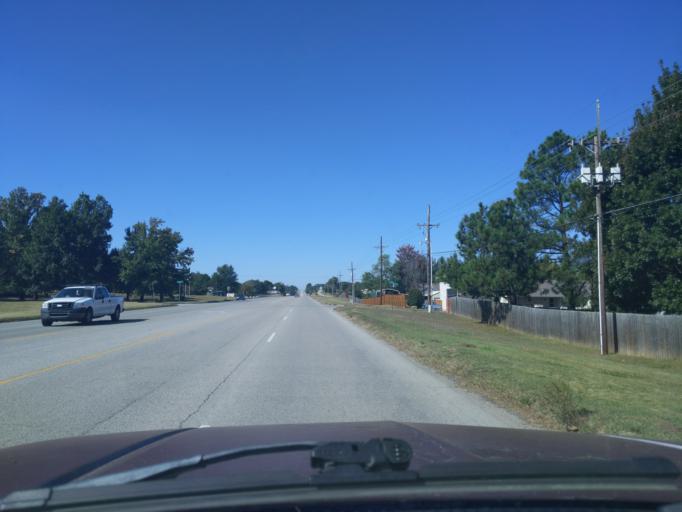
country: US
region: Oklahoma
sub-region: Creek County
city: Kiefer
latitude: 35.9885
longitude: -96.0704
